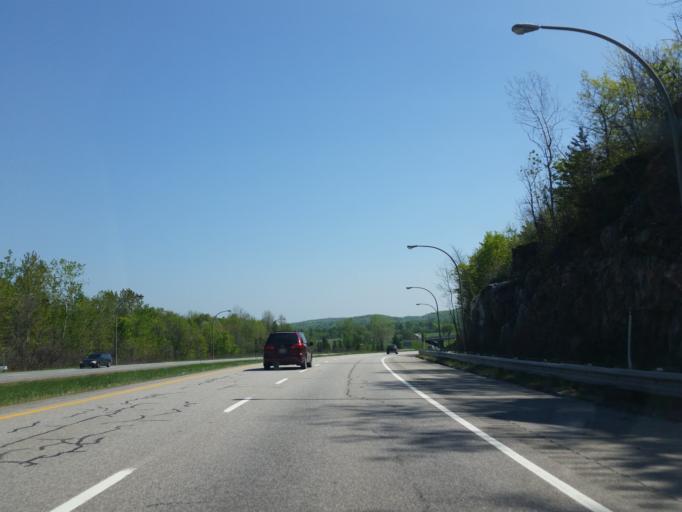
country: CA
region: Quebec
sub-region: Outaouais
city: Gatineau
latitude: 45.5078
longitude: -75.8000
